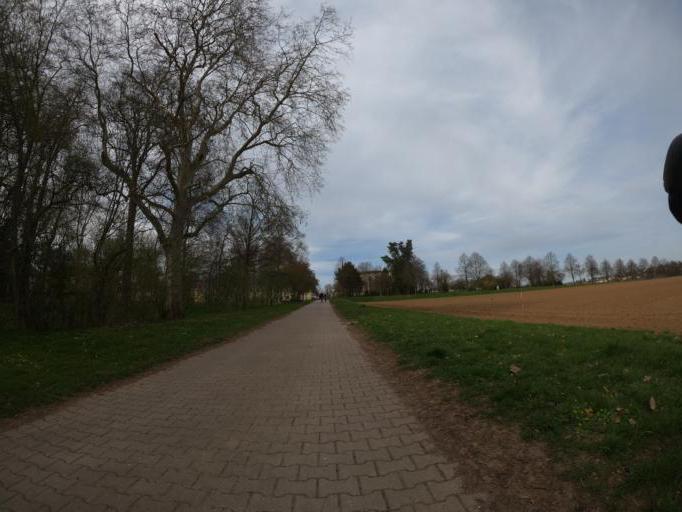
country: DE
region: Baden-Wuerttemberg
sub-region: Regierungsbezirk Stuttgart
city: Ostfildern
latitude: 48.7112
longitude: 9.2170
